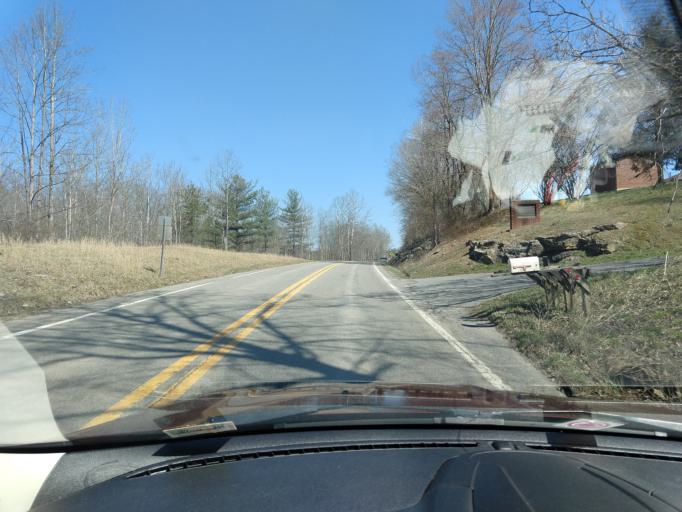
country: US
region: West Virginia
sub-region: Braxton County
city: Sutton
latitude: 38.6929
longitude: -80.6720
